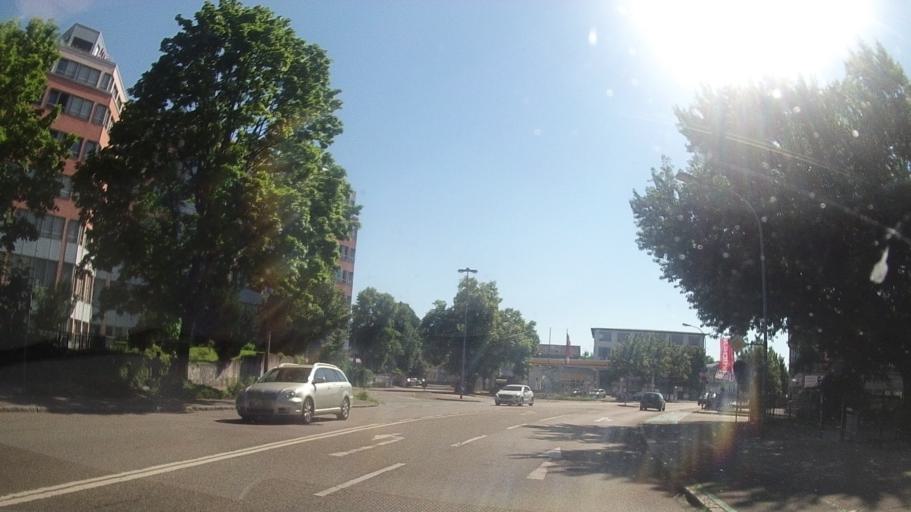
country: DE
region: Baden-Wuerttemberg
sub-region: Freiburg Region
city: Offenburg
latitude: 48.4762
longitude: 7.9428
